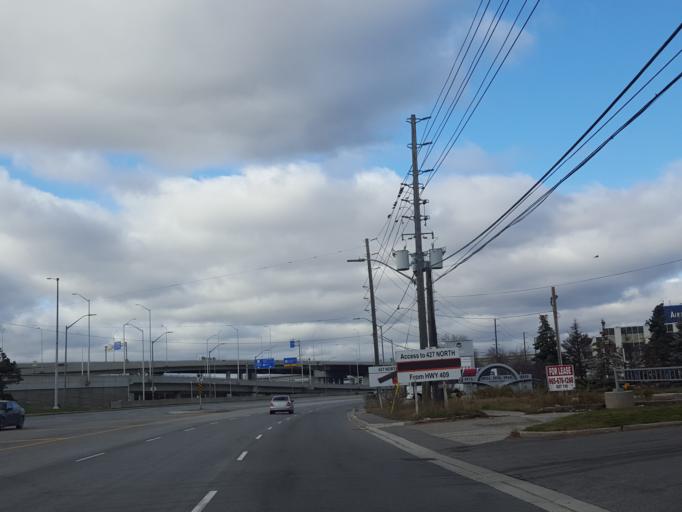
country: CA
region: Ontario
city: Etobicoke
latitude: 43.6859
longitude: -79.6075
